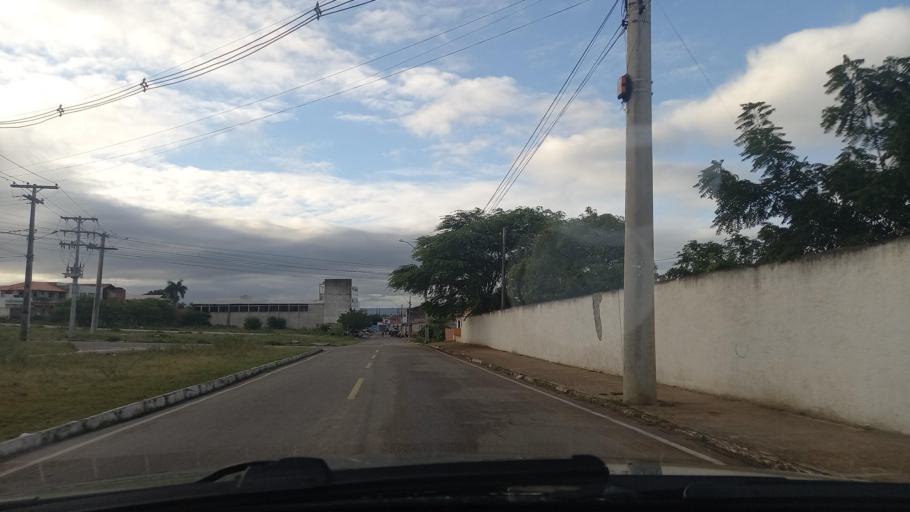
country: BR
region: Bahia
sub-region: Paulo Afonso
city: Paulo Afonso
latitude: -9.3900
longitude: -38.2320
